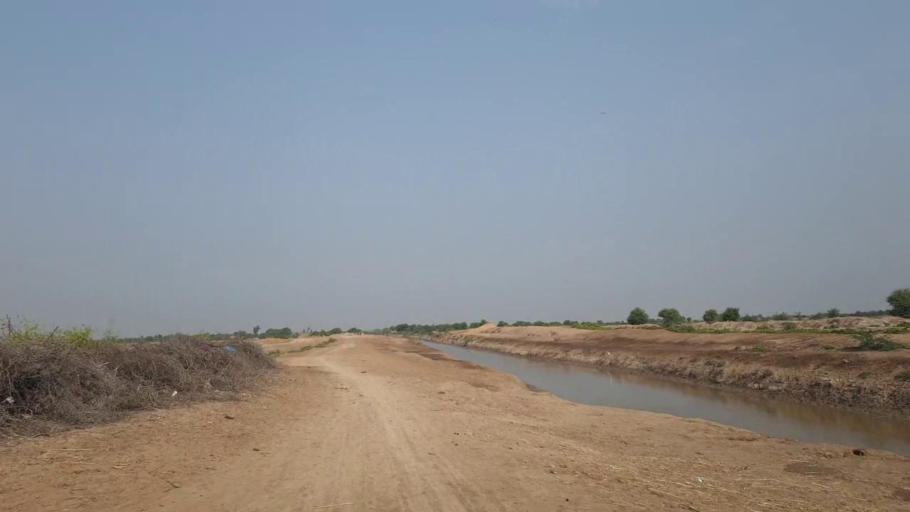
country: PK
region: Sindh
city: Badin
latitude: 24.7285
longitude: 68.7681
